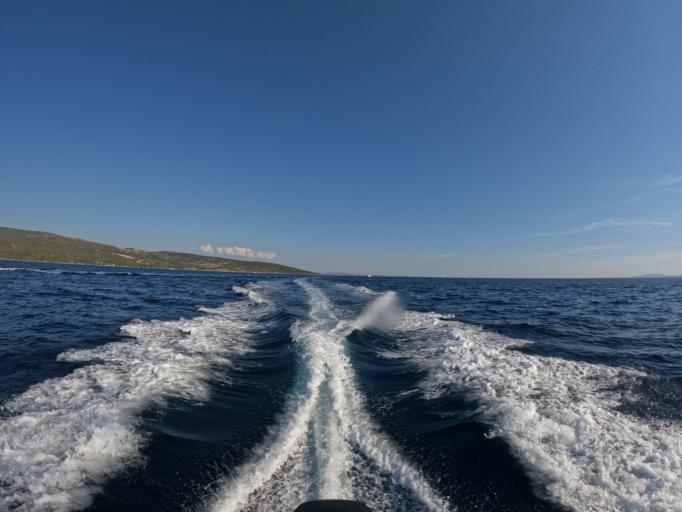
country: HR
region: Primorsko-Goranska
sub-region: Grad Krk
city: Krk
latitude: 45.0015
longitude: 14.5971
